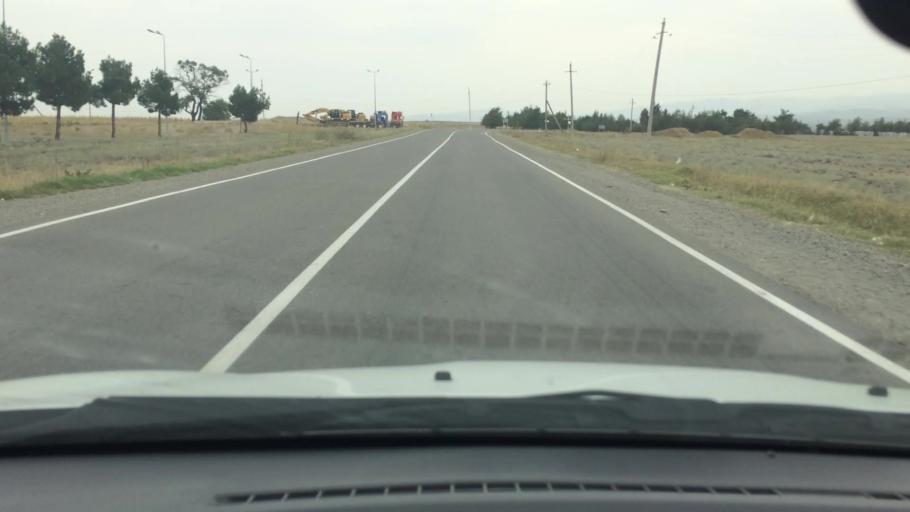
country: GE
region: Kvemo Kartli
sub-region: Gardabani
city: Gardabani
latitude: 41.3497
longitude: 45.0675
